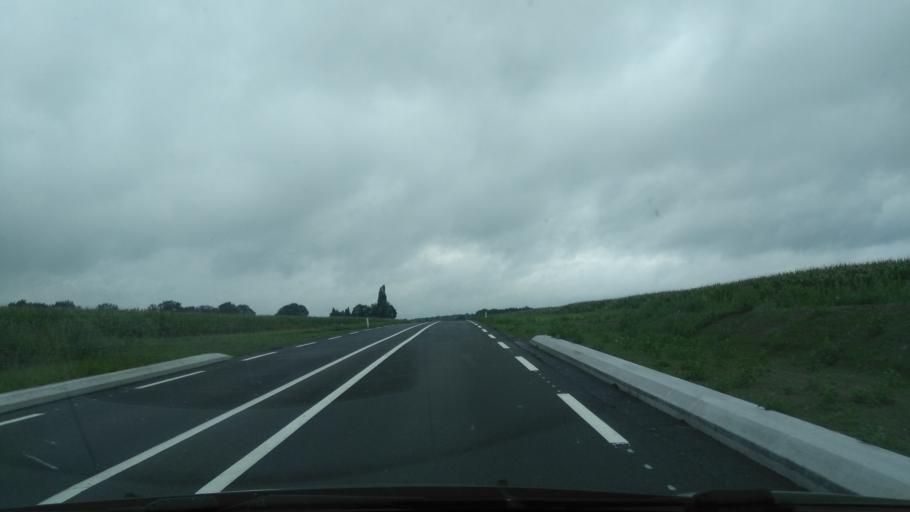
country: NL
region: North Brabant
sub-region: Gemeente Baarle-Nassau
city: Baarle-Nassau
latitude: 51.4485
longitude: 4.9442
